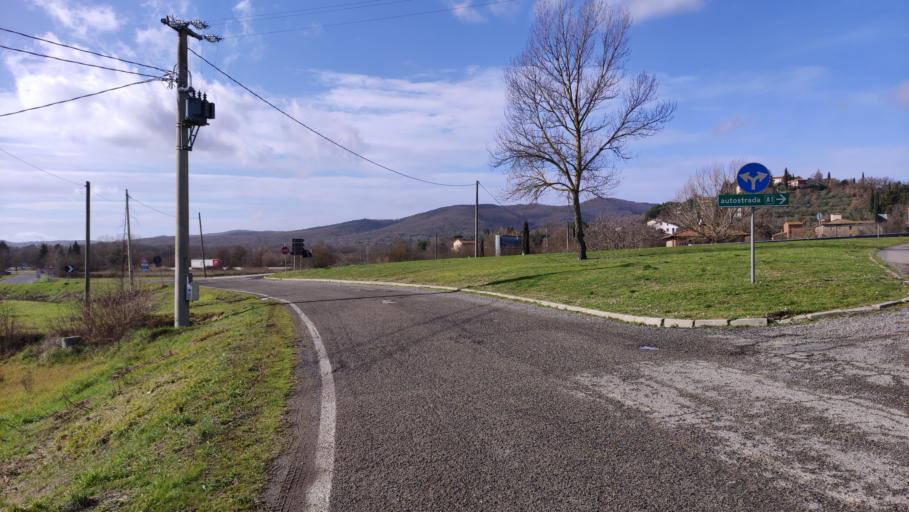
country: IT
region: Tuscany
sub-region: Province of Arezzo
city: Viciomaggio
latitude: 43.4224
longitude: 11.7775
